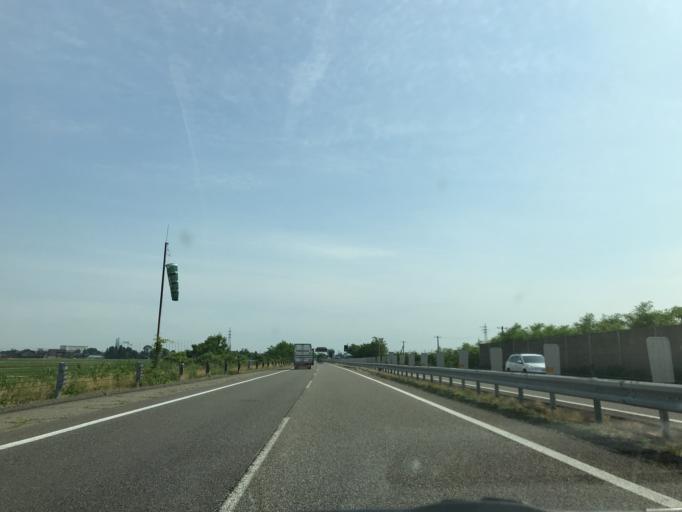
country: JP
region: Niigata
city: Sanjo
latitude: 37.6164
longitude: 138.9202
